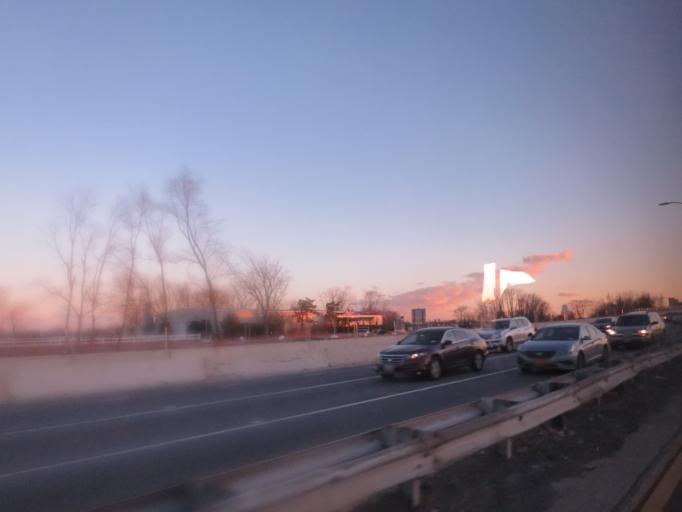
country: US
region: New York
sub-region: Kings County
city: East New York
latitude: 40.6082
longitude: -73.8979
